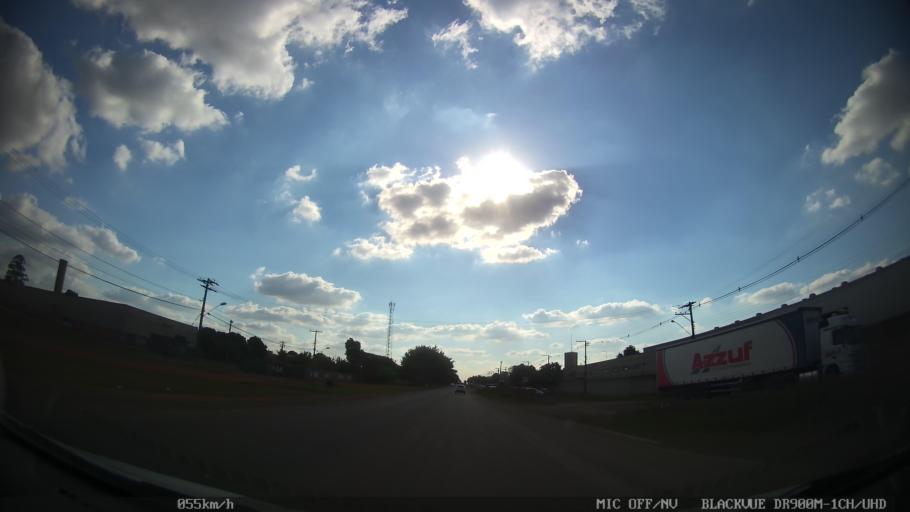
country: BR
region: Sao Paulo
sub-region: Santa Barbara D'Oeste
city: Santa Barbara d'Oeste
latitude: -22.7750
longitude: -47.3786
